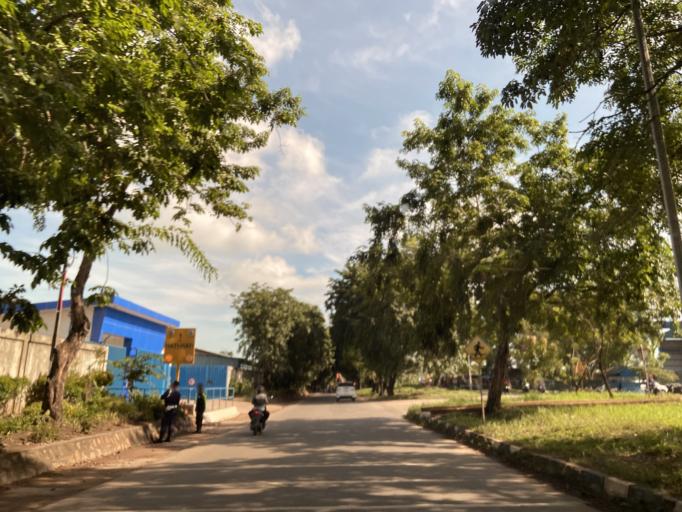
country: SG
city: Singapore
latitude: 1.1667
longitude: 104.0117
